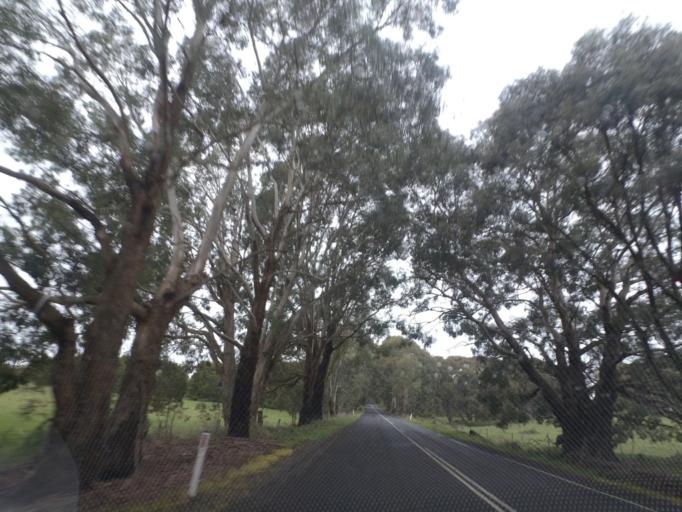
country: AU
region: Victoria
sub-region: Hume
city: Sunbury
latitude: -37.3458
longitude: 144.6057
